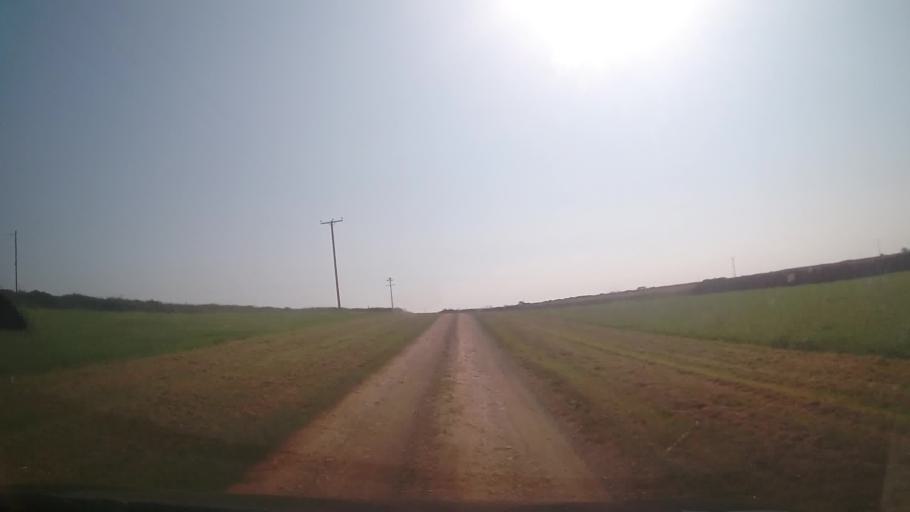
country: GB
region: Wales
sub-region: Pembrokeshire
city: Llanrhian
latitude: 51.9244
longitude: -5.2190
